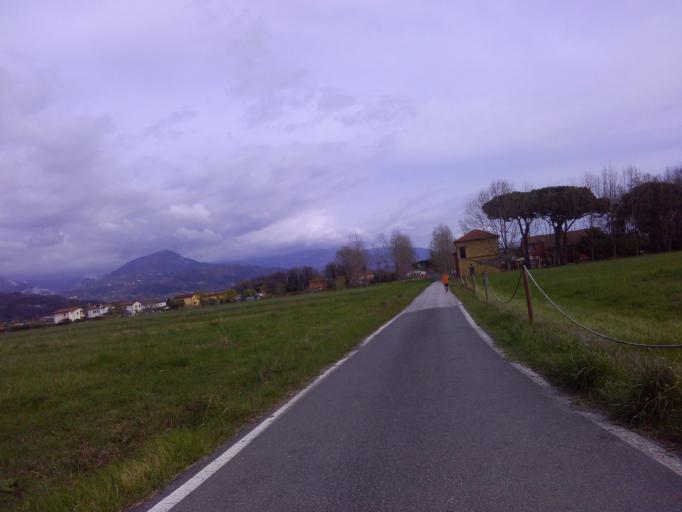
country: IT
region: Liguria
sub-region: Provincia di La Spezia
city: Casano-Dogana-Isola
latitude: 44.0564
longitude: 10.0271
